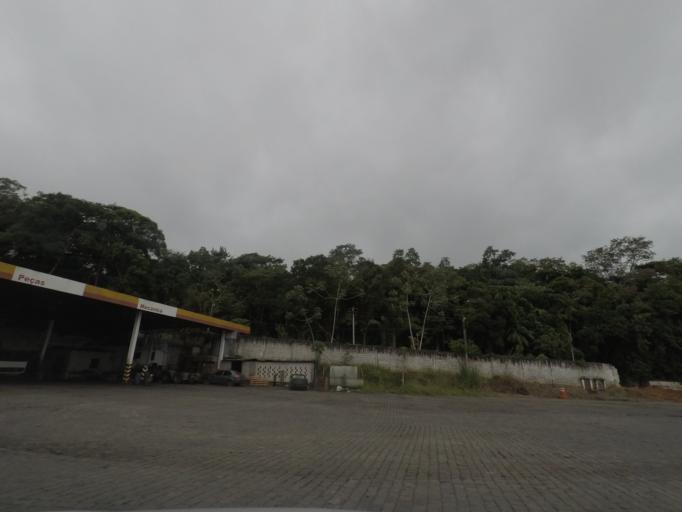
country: BR
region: Sao Paulo
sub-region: Jacupiranga
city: Jacupiranga
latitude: -24.6516
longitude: -47.9398
